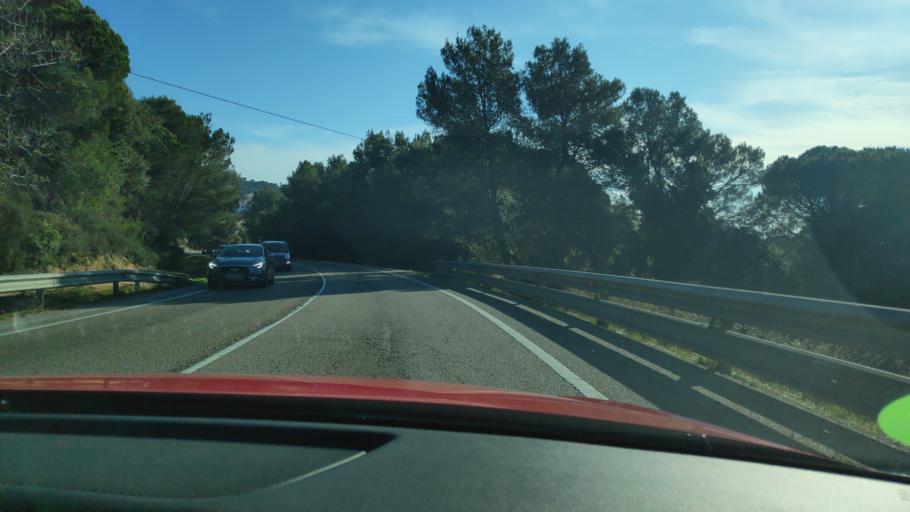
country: ES
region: Catalonia
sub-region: Provincia de Girona
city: Lloret de Mar
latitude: 41.7183
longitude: 2.8263
